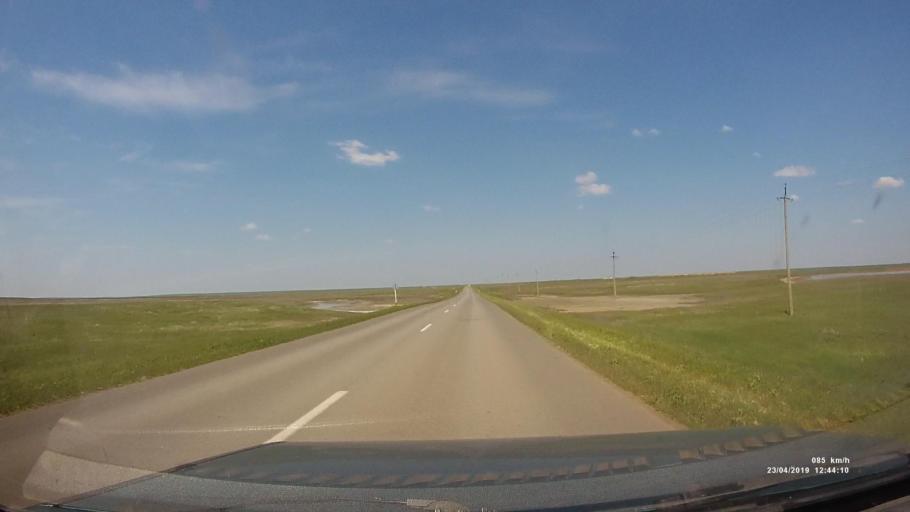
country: RU
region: Kalmykiya
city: Yashalta
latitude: 46.4734
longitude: 42.6488
